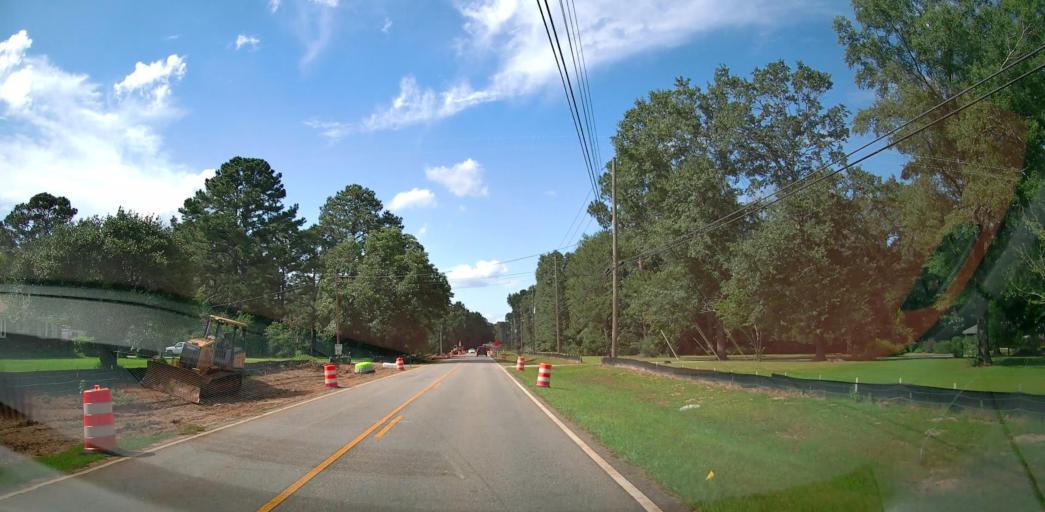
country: US
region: Georgia
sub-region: Houston County
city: Perry
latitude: 32.4855
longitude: -83.7016
